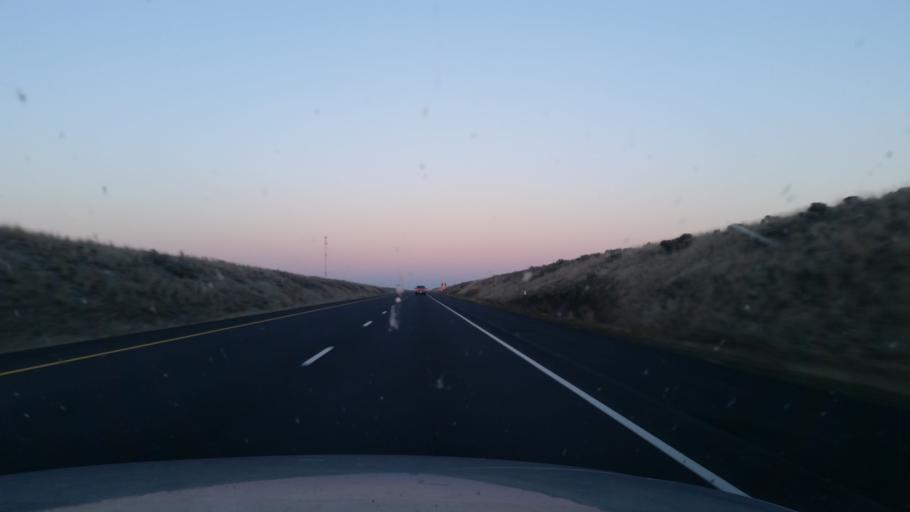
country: US
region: Washington
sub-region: Adams County
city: Ritzville
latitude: 47.0915
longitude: -118.6999
